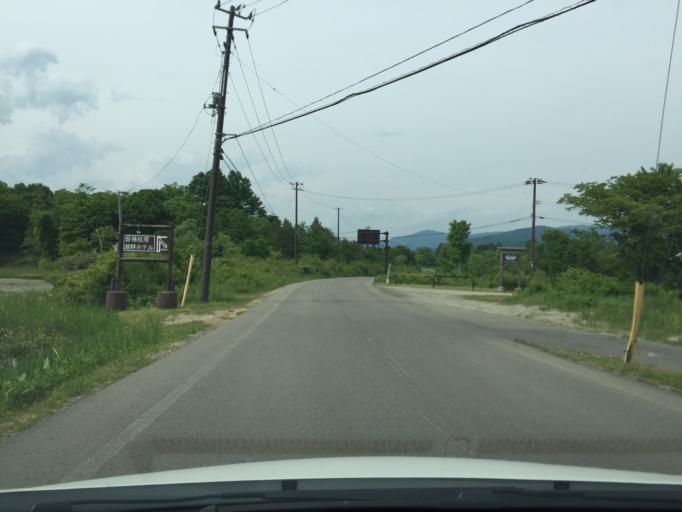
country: JP
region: Fukushima
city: Inawashiro
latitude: 37.6666
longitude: 140.0455
